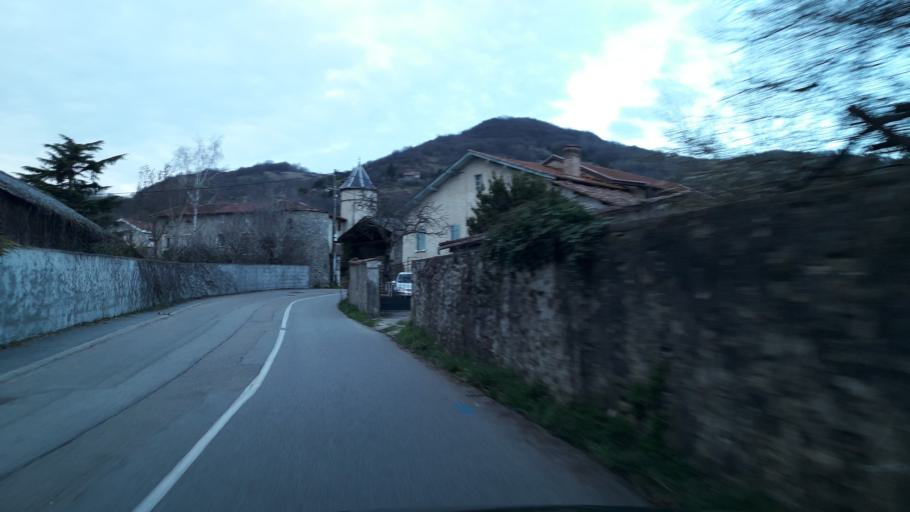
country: FR
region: Rhone-Alpes
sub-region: Departement de l'Isere
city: Brie-et-Angonnes
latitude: 45.1402
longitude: 5.7779
